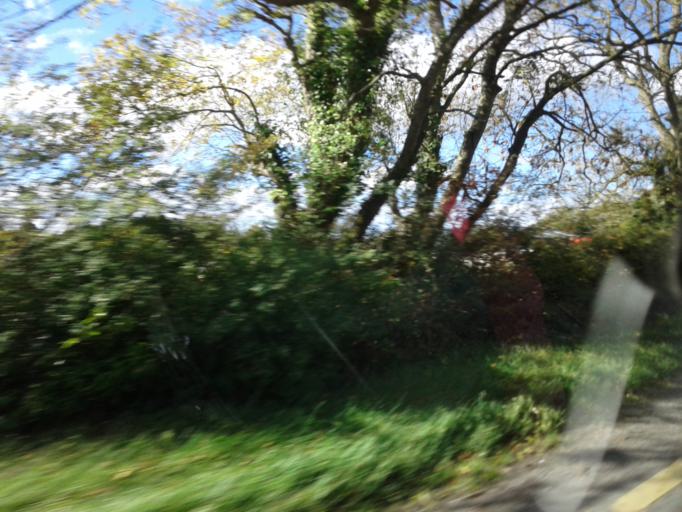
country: IE
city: Kentstown
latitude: 53.6507
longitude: -6.5148
